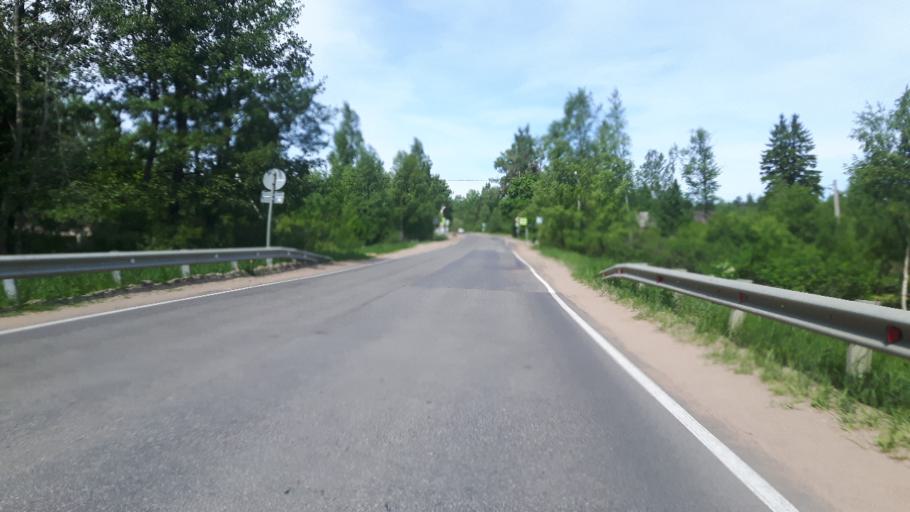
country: RU
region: Leningrad
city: Ust'-Luga
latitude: 59.6551
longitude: 28.2554
